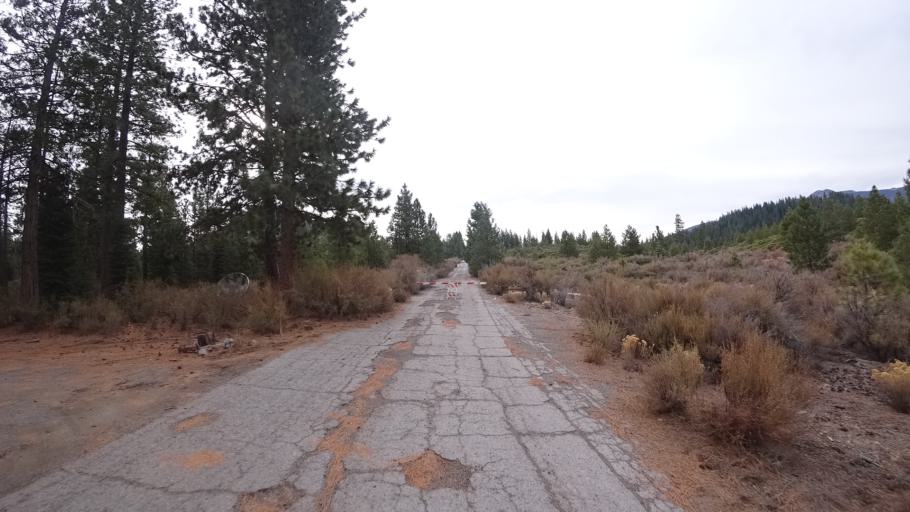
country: US
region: California
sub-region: Siskiyou County
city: Weed
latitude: 41.3929
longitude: -122.3728
